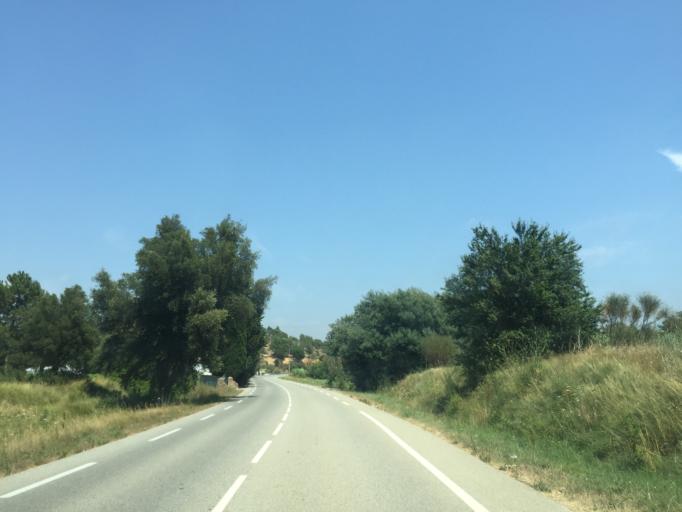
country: FR
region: Provence-Alpes-Cote d'Azur
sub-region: Departement du Var
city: Puget-sur-Argens
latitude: 43.4016
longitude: 6.6791
